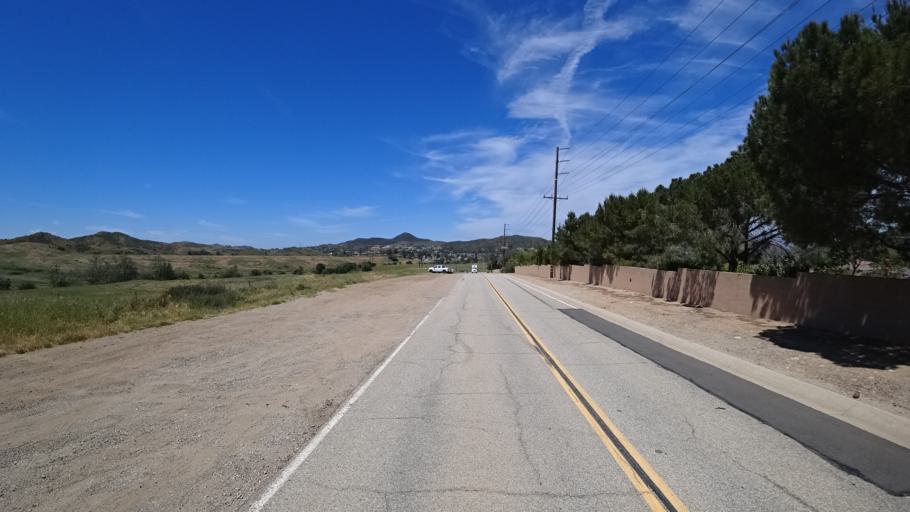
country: US
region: California
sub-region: Ventura County
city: Casa Conejo
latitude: 34.1549
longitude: -118.9521
